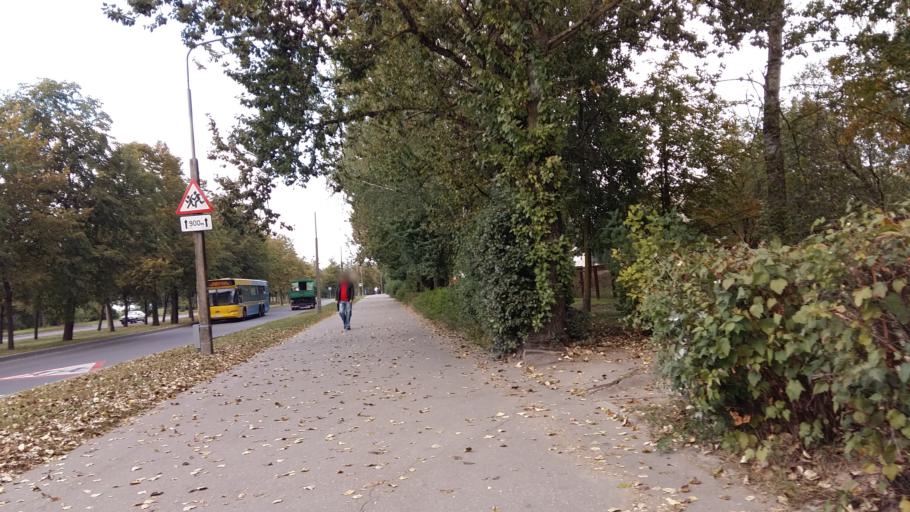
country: BY
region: Grodnenskaya
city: Hrodna
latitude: 53.7004
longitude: 23.7988
